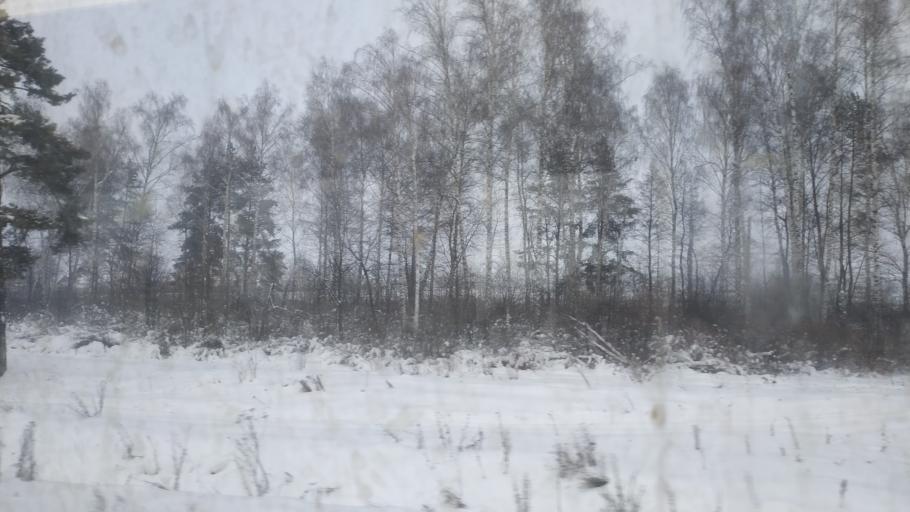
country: RU
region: Moskovskaya
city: Malyshevo
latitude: 55.5246
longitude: 38.3228
